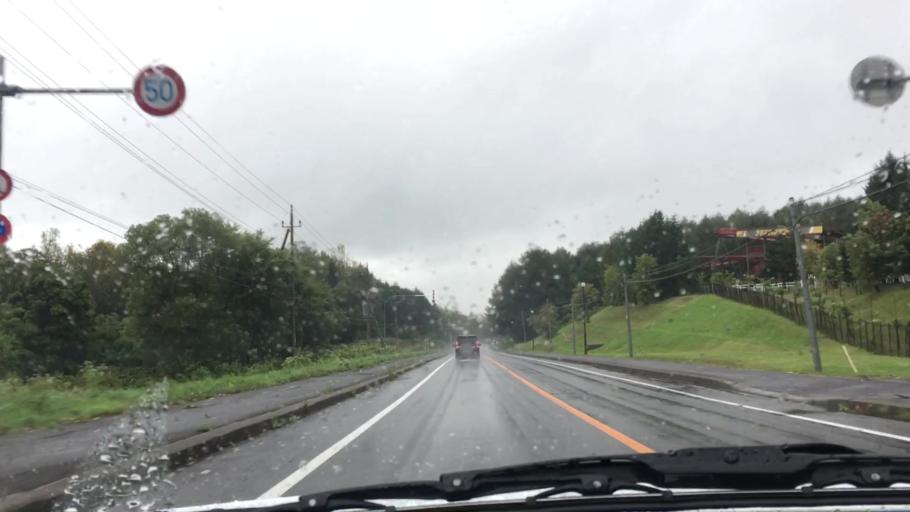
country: JP
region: Hokkaido
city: Niseko Town
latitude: 42.7466
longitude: 140.8975
